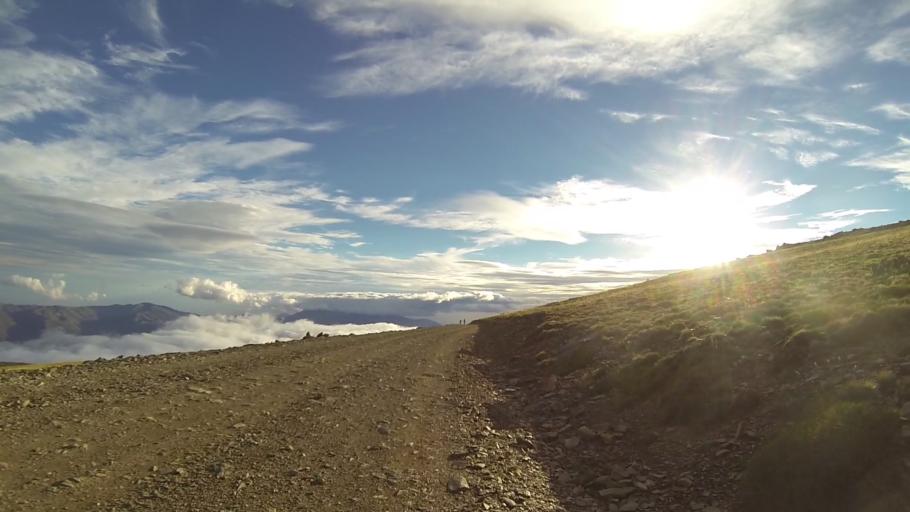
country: ES
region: Andalusia
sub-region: Provincia de Granada
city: Portugos
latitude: 36.9859
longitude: -3.3142
